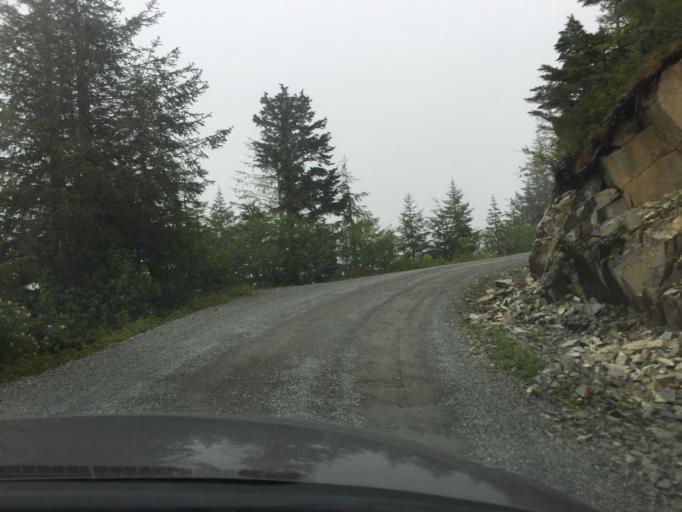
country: US
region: Alaska
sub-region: Sitka City and Borough
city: Sitka
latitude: 57.0967
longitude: -135.3662
